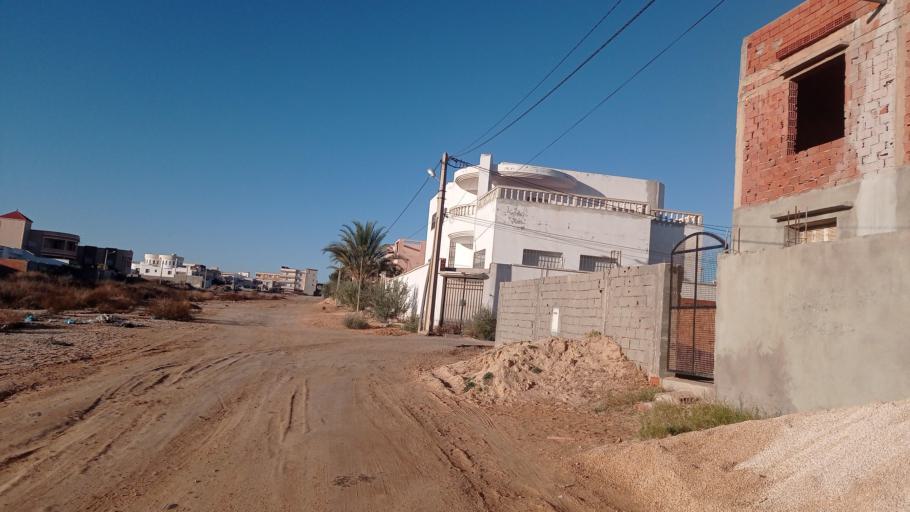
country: TN
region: Qabis
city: Gabes
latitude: 33.8493
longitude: 10.1170
